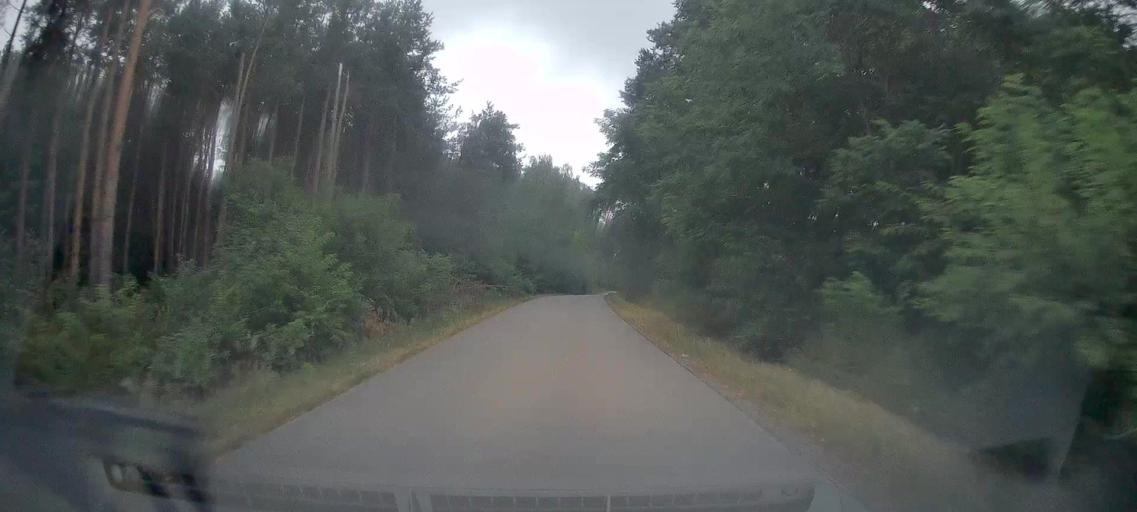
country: PL
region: Masovian Voivodeship
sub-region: Powiat radomski
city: Jedlinsk
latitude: 51.4601
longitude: 21.1050
